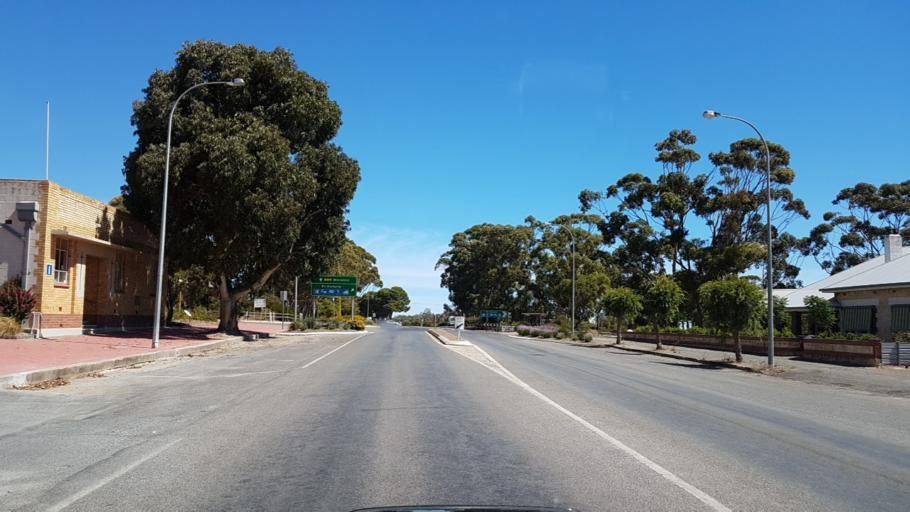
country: AU
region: South Australia
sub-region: Yorke Peninsula
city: Maitland
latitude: -34.3760
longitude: 137.6721
